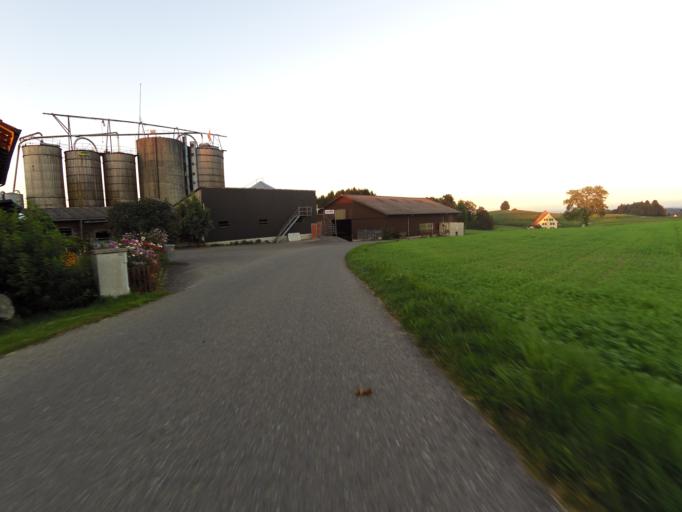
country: CH
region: Thurgau
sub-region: Weinfelden District
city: Wigoltingen
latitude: 47.5670
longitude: 9.0370
